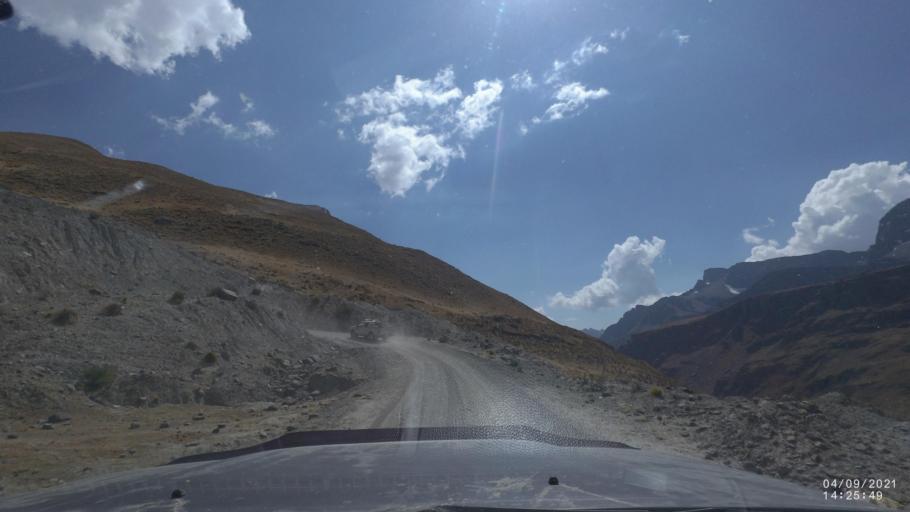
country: BO
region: Cochabamba
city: Sipe Sipe
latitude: -17.2422
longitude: -66.4092
